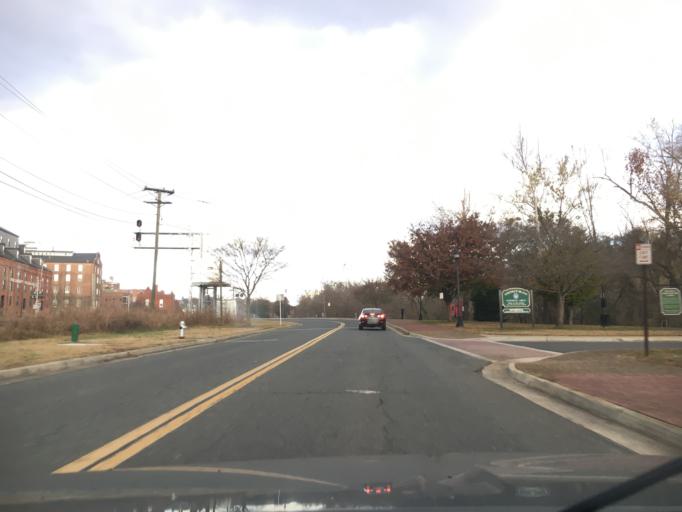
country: US
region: Virginia
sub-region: City of Lynchburg
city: Lynchburg
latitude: 37.4104
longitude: -79.1353
